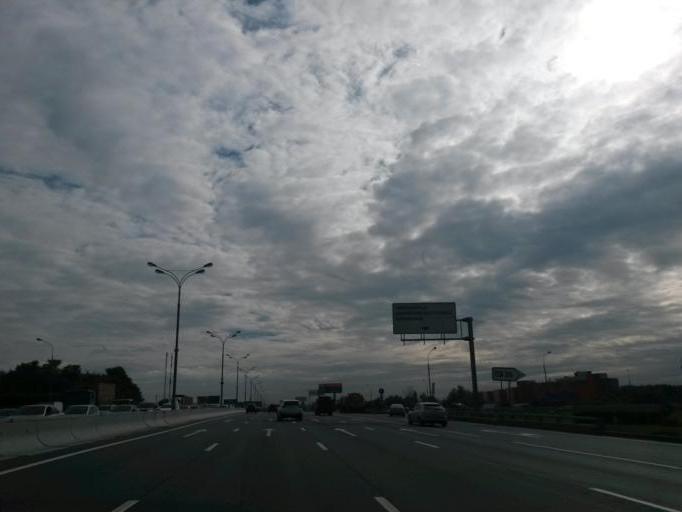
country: RU
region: Moscow
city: Biryulevo
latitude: 55.5760
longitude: 37.6883
